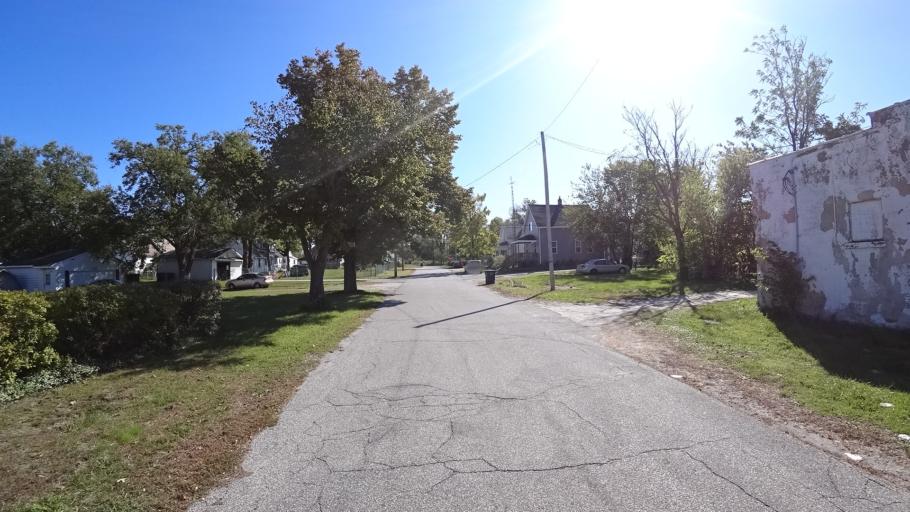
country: US
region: Indiana
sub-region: LaPorte County
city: Michigan City
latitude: 41.7039
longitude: -86.9129
